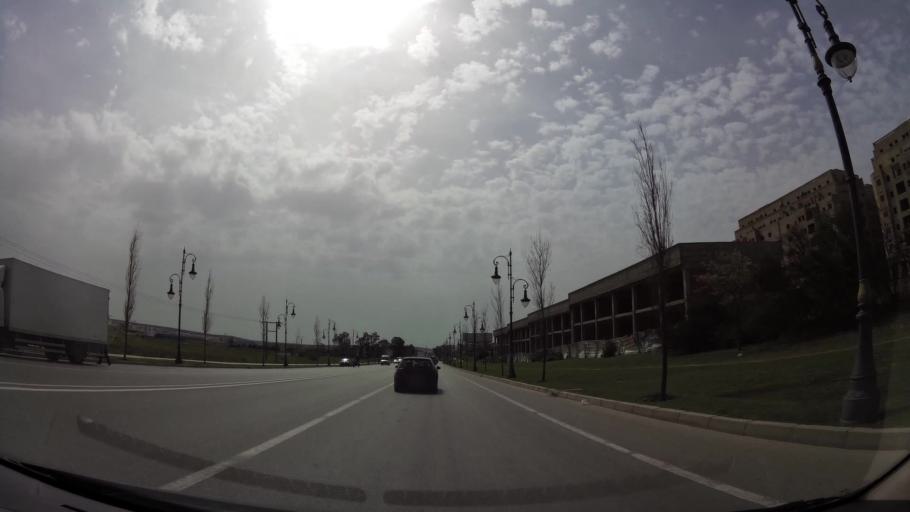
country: MA
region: Tanger-Tetouan
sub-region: Tanger-Assilah
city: Boukhalef
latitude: 35.7327
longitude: -5.8714
